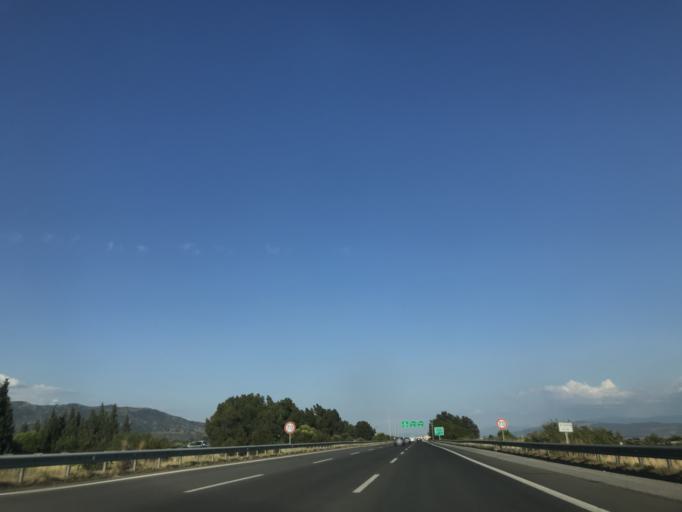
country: TR
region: Aydin
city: Acarlar
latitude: 37.8620
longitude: 27.7797
